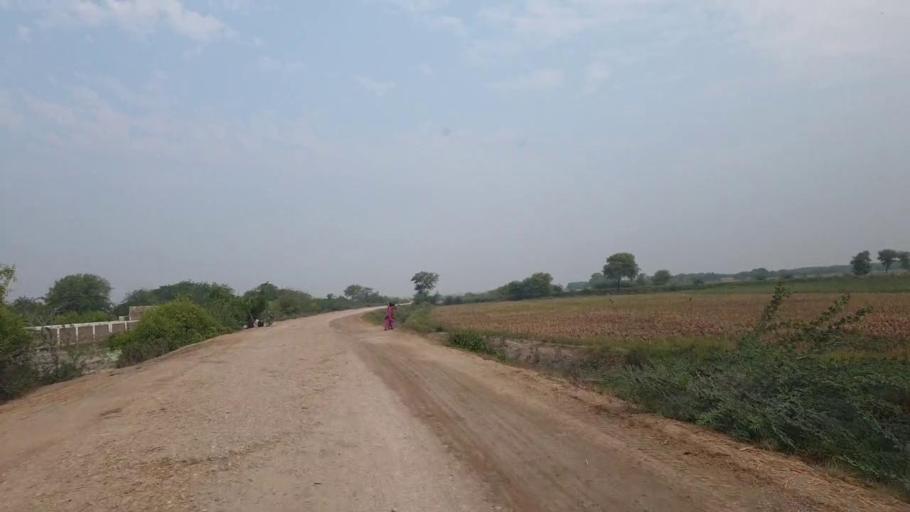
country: PK
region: Sindh
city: Tando Bago
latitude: 24.7967
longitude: 68.8760
